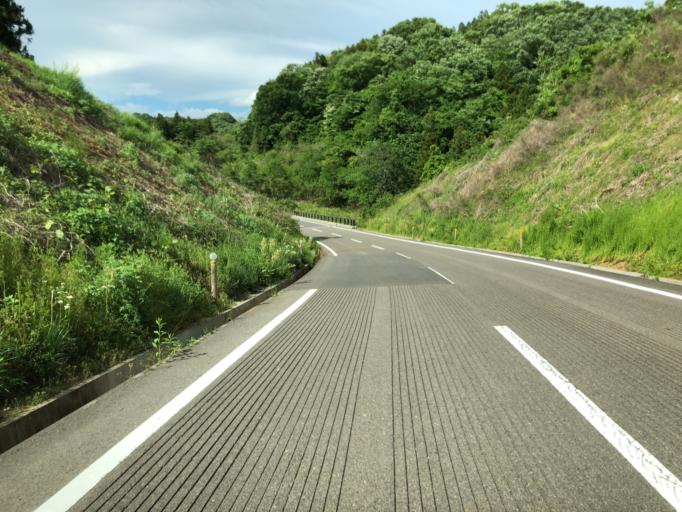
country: JP
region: Fukushima
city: Nihommatsu
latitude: 37.6003
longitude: 140.5192
